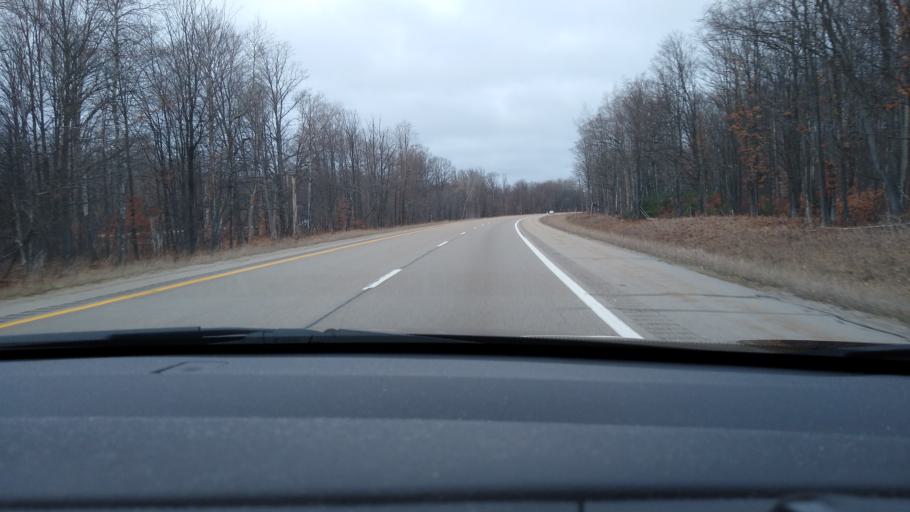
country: US
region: Michigan
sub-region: Crawford County
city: Grayling
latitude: 44.8255
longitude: -84.7131
